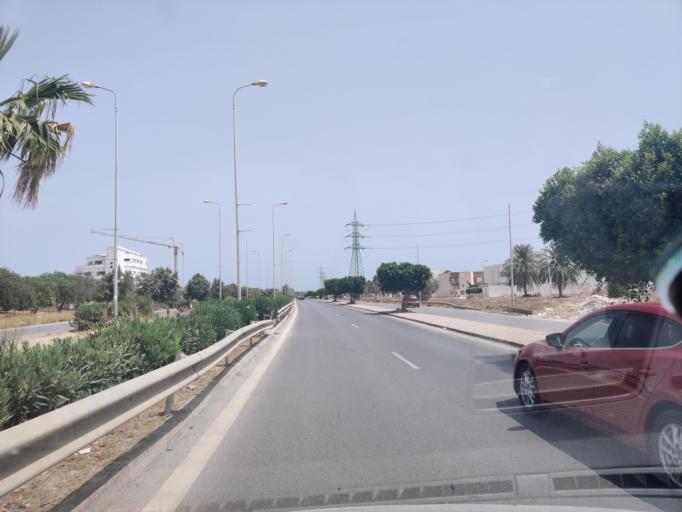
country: TN
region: Tunis
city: La Goulette
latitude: 36.8459
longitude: 10.3020
